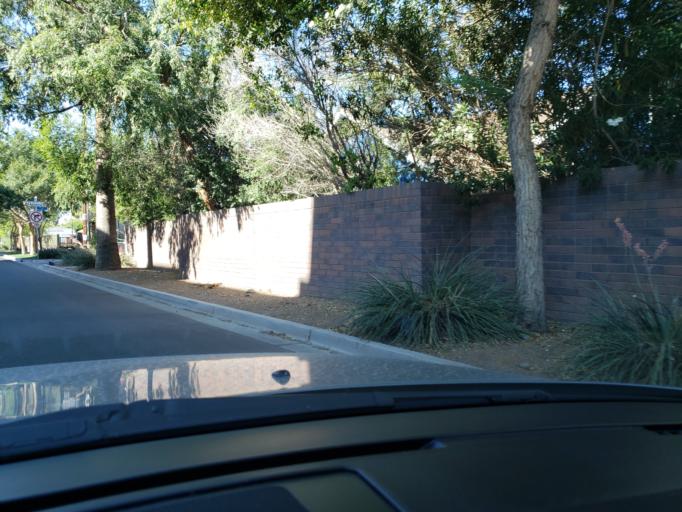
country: US
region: Arizona
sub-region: Maricopa County
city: Phoenix
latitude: 33.4671
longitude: -112.0759
